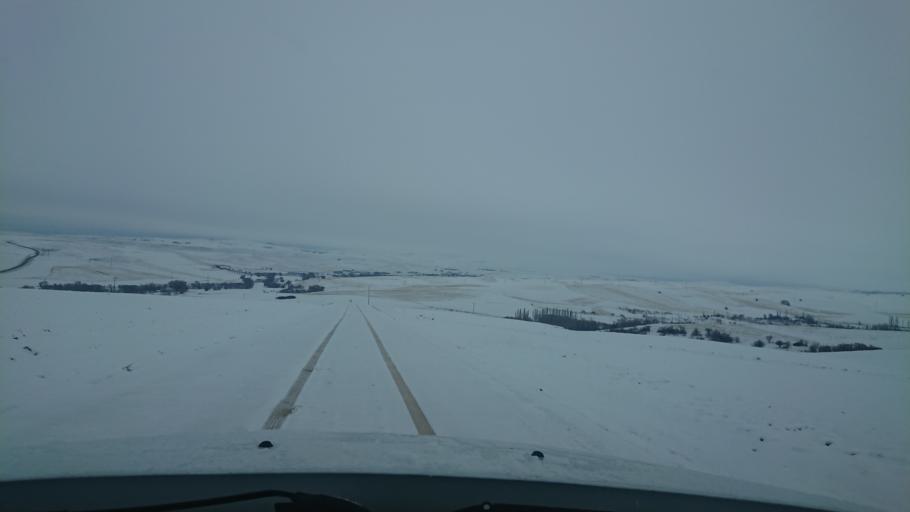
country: TR
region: Aksaray
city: Agacoren
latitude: 38.7518
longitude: 33.8754
